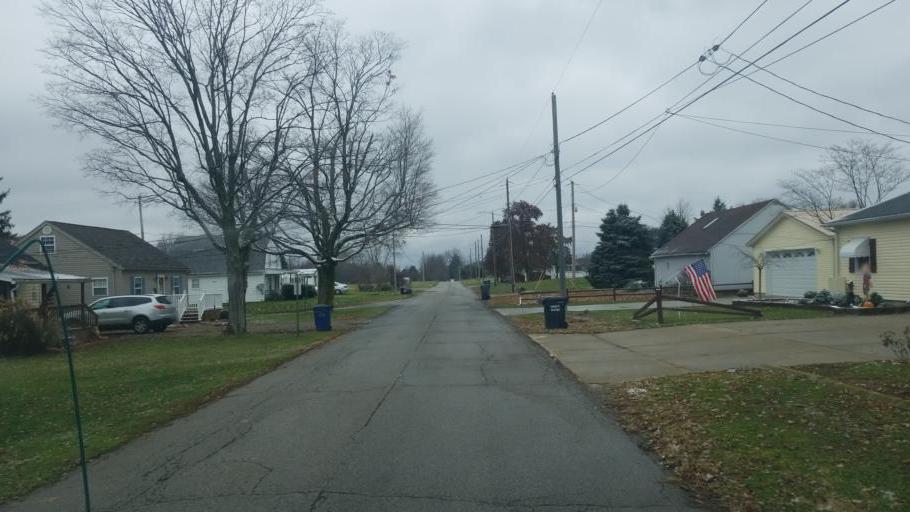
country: US
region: Ohio
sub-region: Richland County
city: Shelby
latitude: 40.8920
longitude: -82.6545
